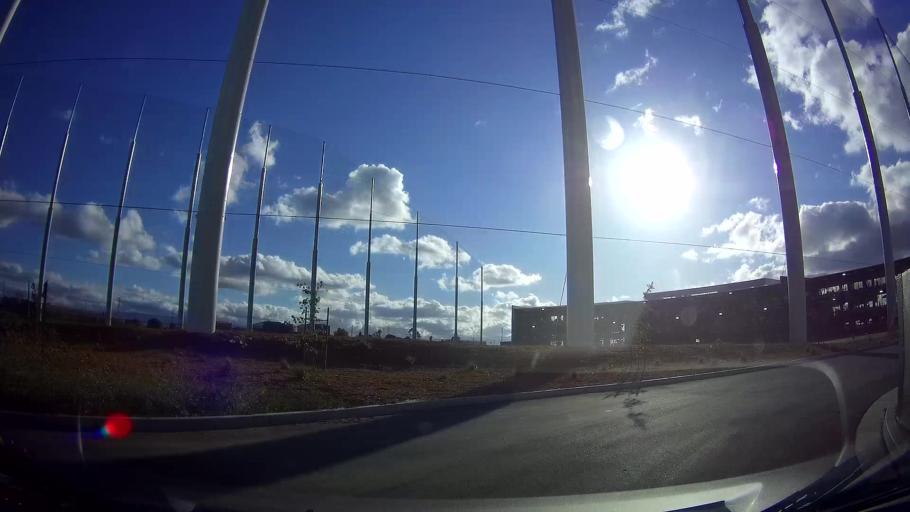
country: US
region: California
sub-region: Santa Clara County
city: Milpitas
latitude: 37.4226
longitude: -121.9682
